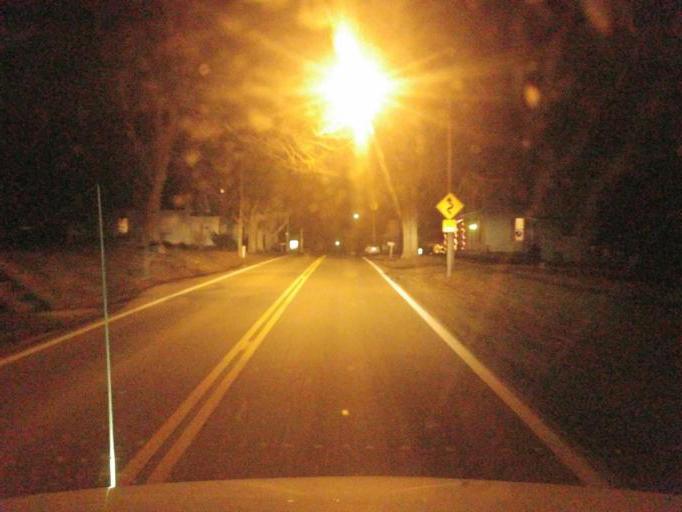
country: US
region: Ohio
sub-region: Harrison County
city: Cadiz
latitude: 40.4028
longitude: -81.0329
